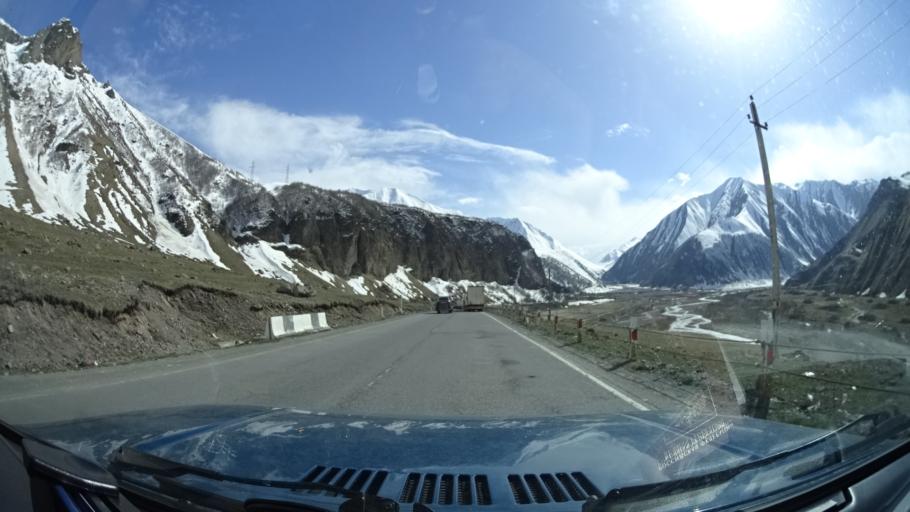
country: GE
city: Gudauri
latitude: 42.5693
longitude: 44.5209
